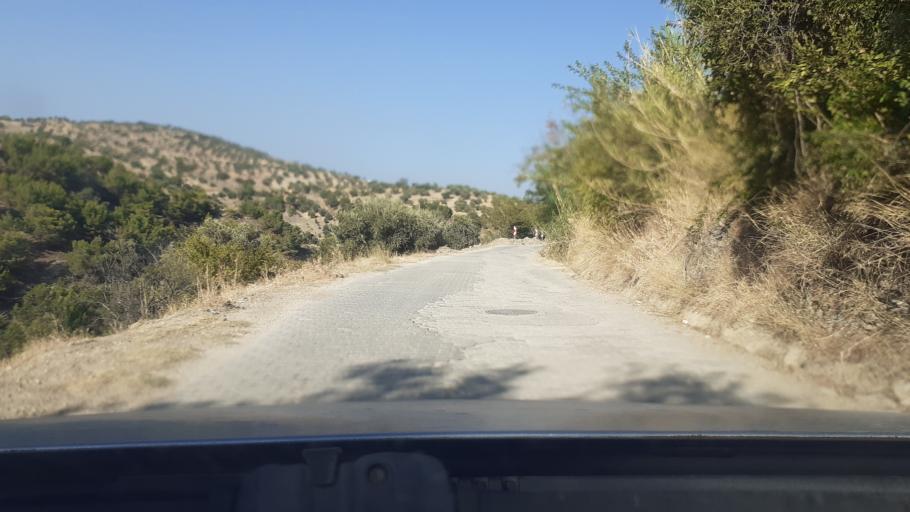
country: TR
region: Hatay
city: Kirikhan
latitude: 36.4881
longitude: 36.2979
